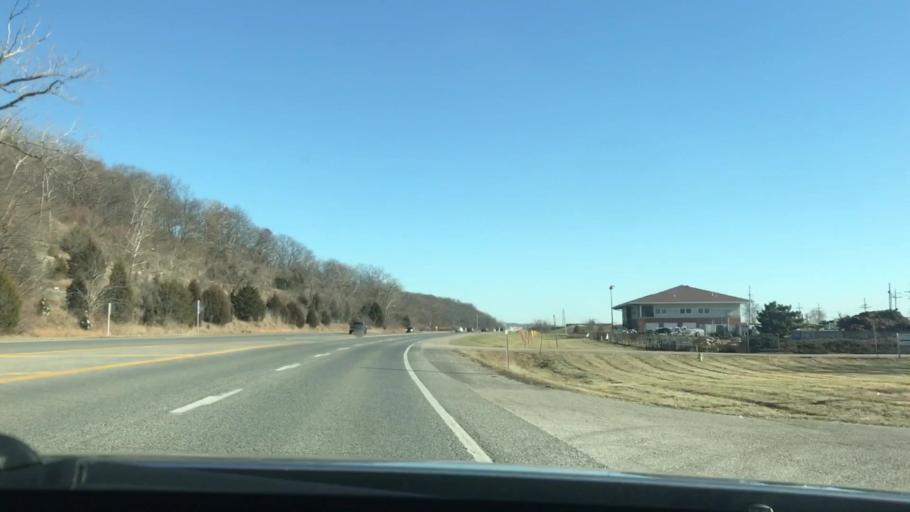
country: US
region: Missouri
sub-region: Platte County
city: Parkville
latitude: 39.1791
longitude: -94.6543
